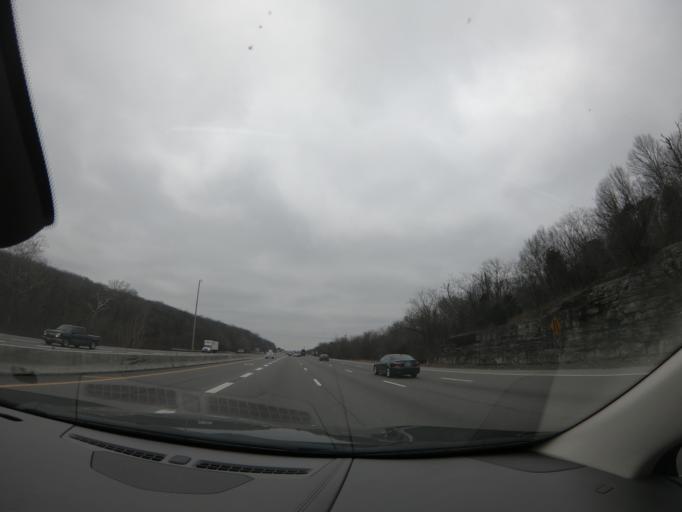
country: US
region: Tennessee
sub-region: Rutherford County
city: La Vergne
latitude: 36.0226
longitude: -86.6296
